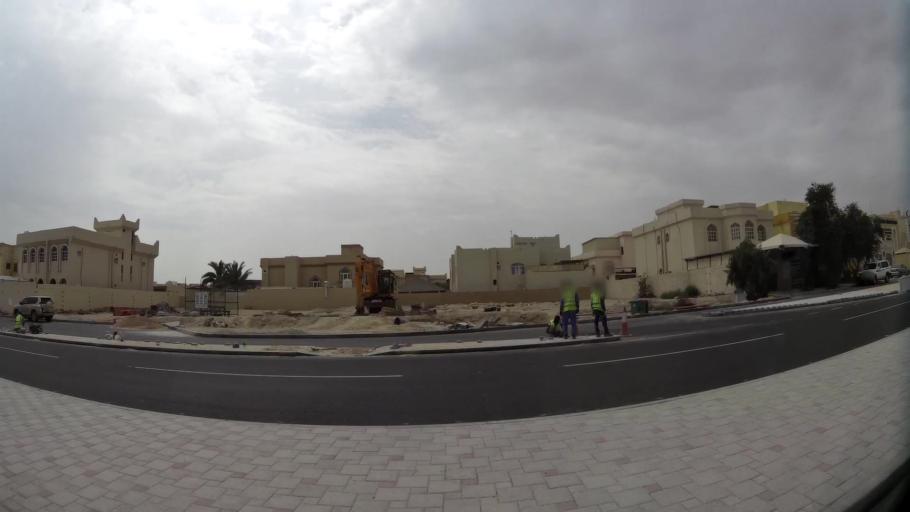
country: QA
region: Baladiyat ar Rayyan
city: Ar Rayyan
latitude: 25.3534
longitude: 51.4653
